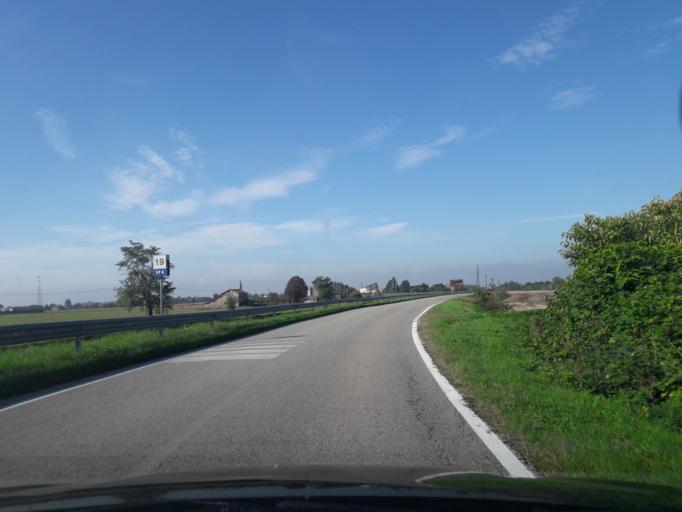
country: IT
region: Veneto
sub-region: Provincia di Rovigo
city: Adria
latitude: 45.0603
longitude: 12.0121
